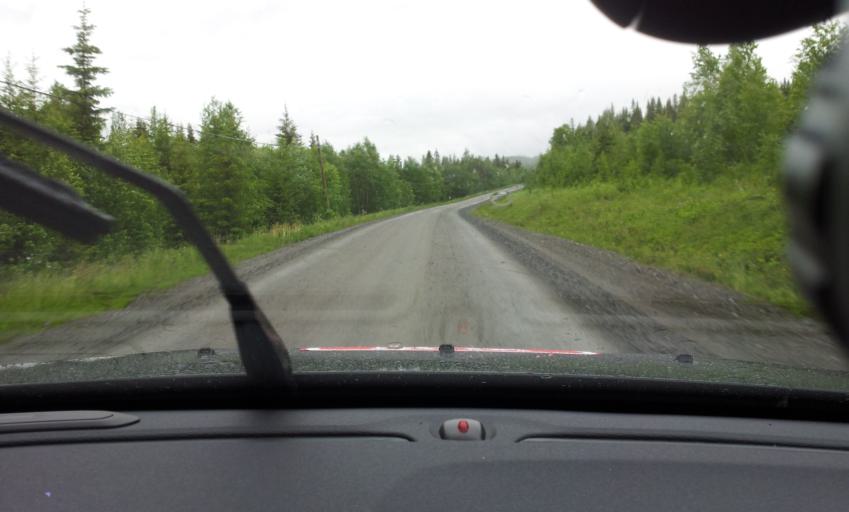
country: SE
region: Jaemtland
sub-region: Are Kommun
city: Are
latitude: 63.4874
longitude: 12.7743
